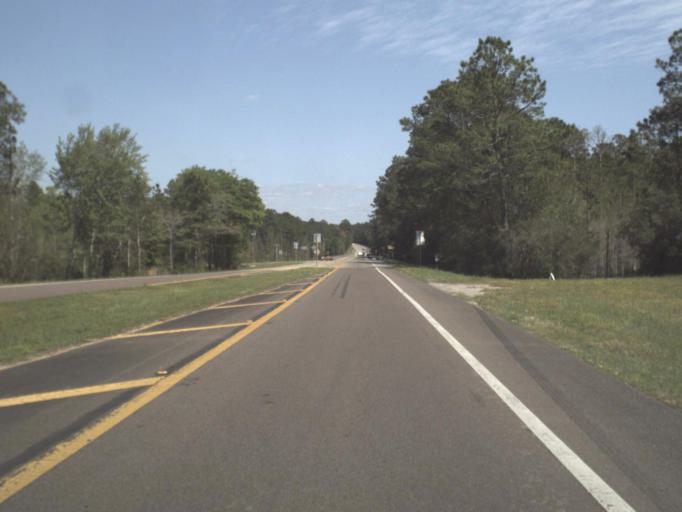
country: US
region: Florida
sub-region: Okaloosa County
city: Crestview
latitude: 30.7541
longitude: -86.5162
